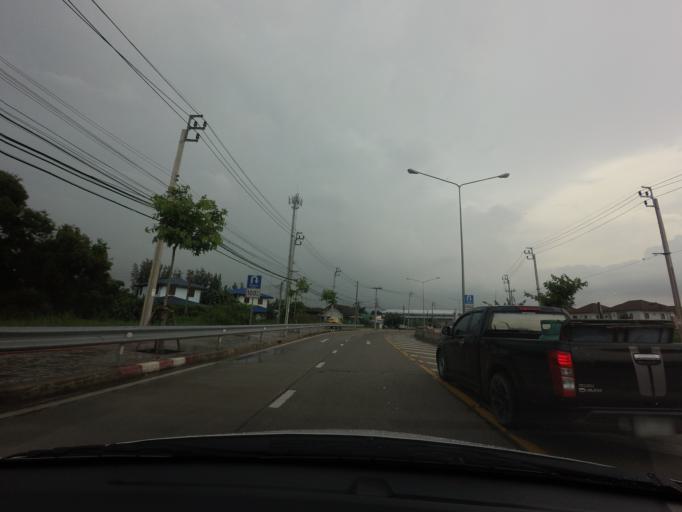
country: TH
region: Bangkok
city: Min Buri
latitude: 13.8182
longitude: 100.7514
